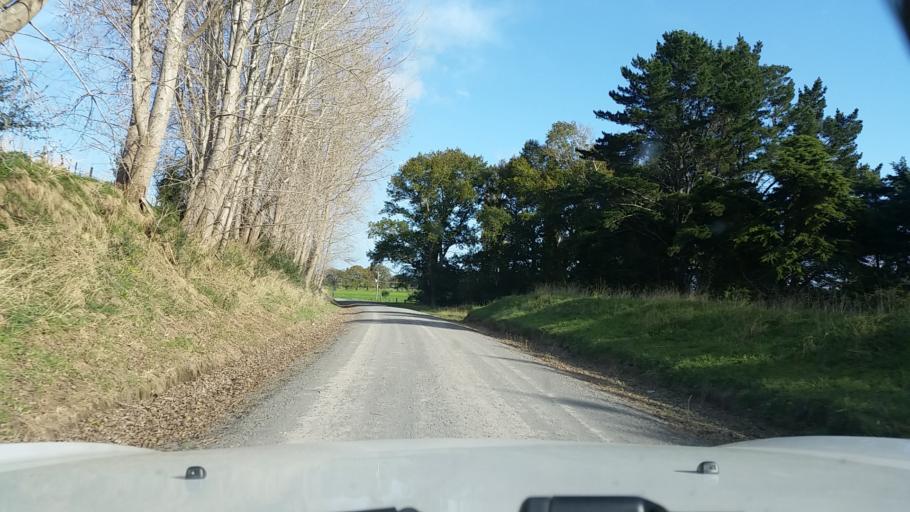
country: NZ
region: Bay of Plenty
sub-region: Western Bay of Plenty District
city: Katikati
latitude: -37.6121
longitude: 175.7958
